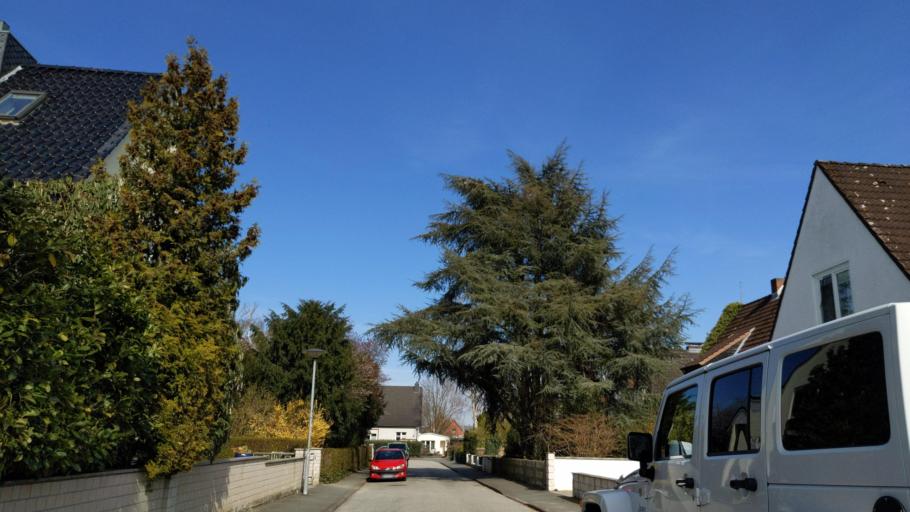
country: DE
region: Schleswig-Holstein
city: Luebeck
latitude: 53.8884
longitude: 10.7161
